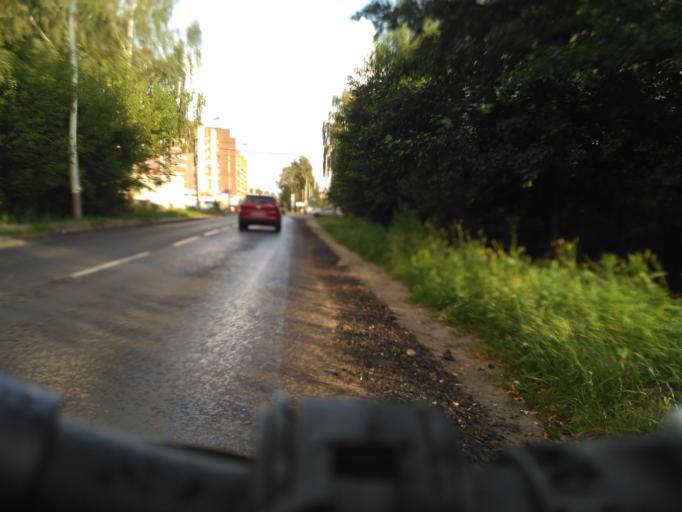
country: RU
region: Moskovskaya
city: Dubna
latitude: 56.7298
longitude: 37.1387
